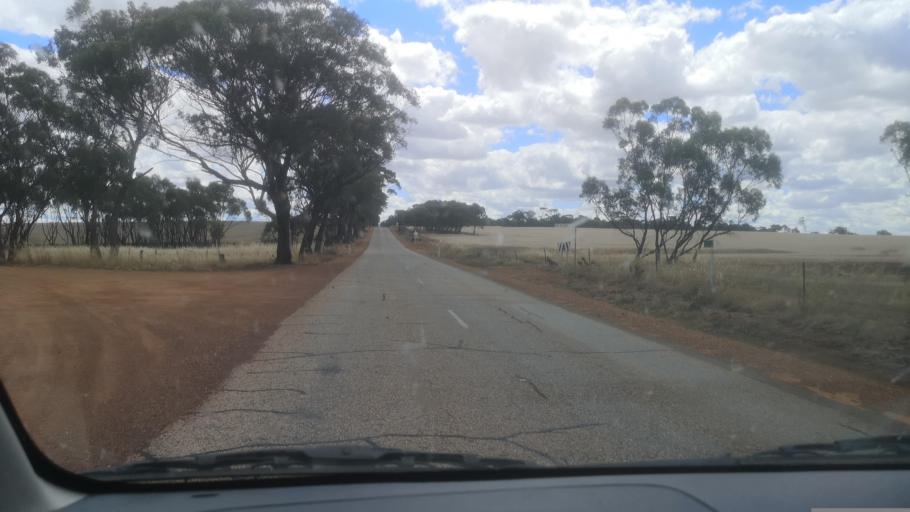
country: AU
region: Western Australia
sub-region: Beverley
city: Beverley
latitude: -31.9899
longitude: 117.1209
